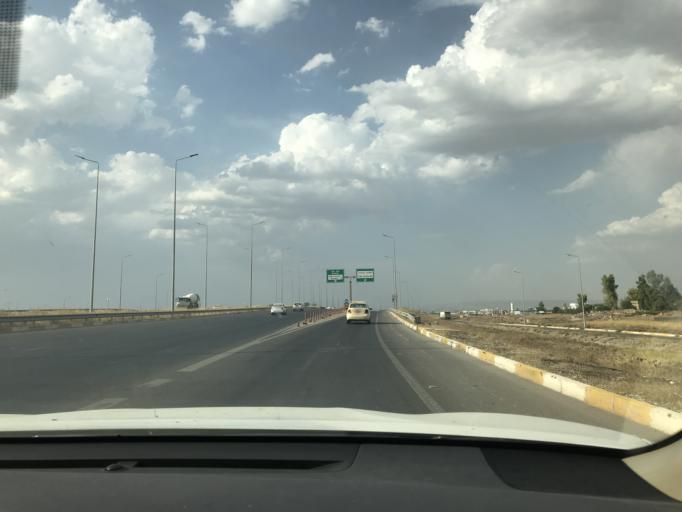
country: IQ
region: Arbil
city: Erbil
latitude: 36.2063
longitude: 43.9529
